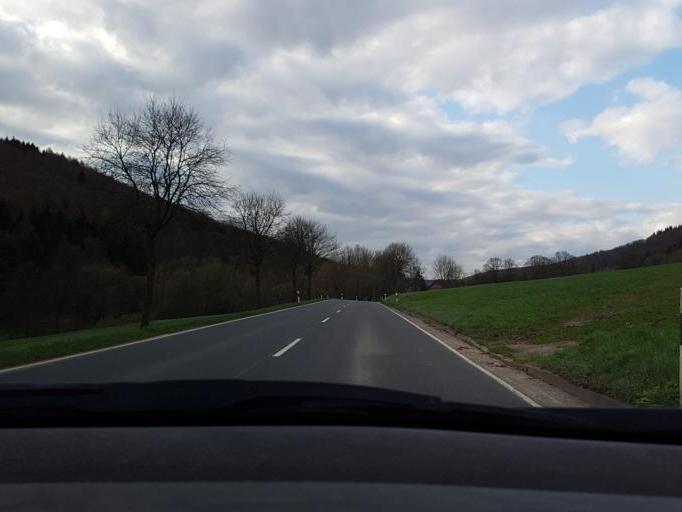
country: DE
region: Lower Saxony
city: Bodenfelde
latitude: 51.6650
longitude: 9.5443
